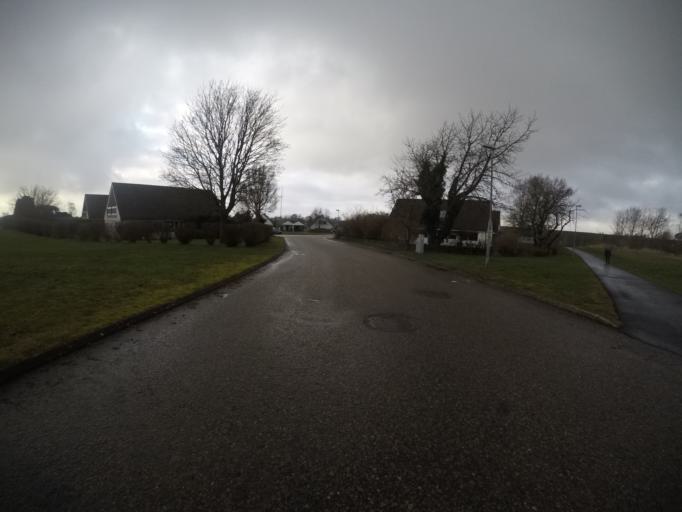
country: SE
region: Halland
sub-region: Laholms Kommun
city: Laholm
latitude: 56.5097
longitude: 13.0276
